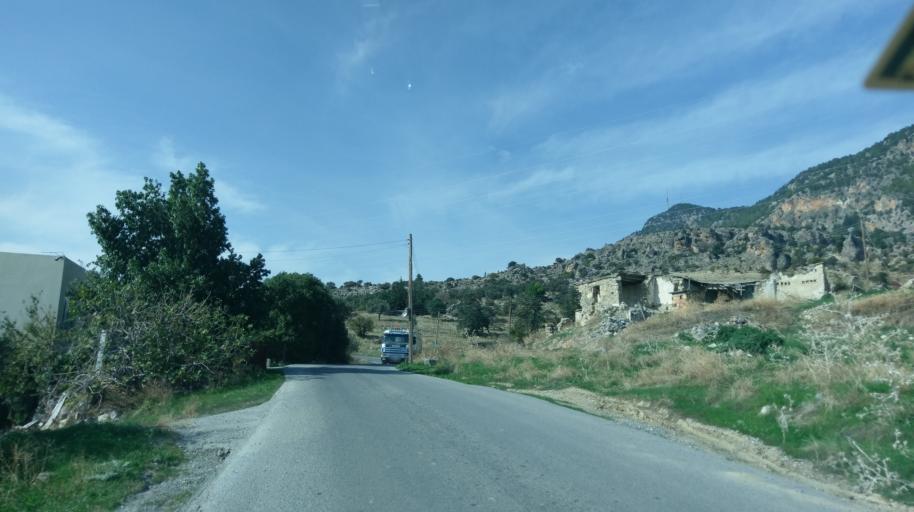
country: CY
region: Keryneia
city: Lapithos
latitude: 35.3011
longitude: 33.1747
